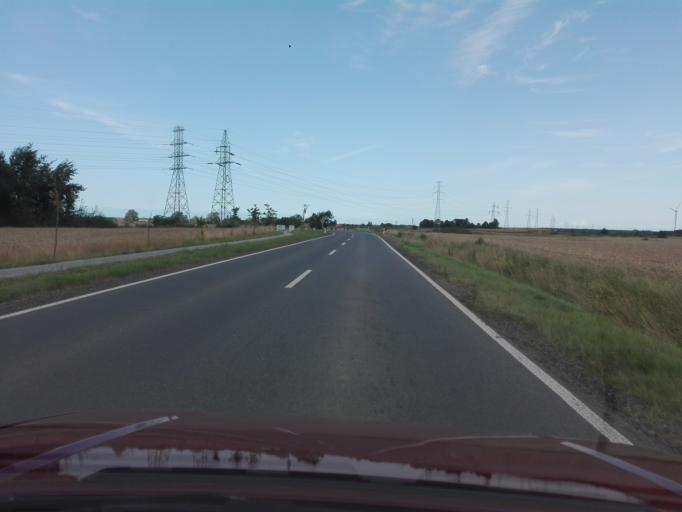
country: PL
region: West Pomeranian Voivodeship
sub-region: Powiat koszalinski
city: Sianow
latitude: 54.3000
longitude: 16.3073
